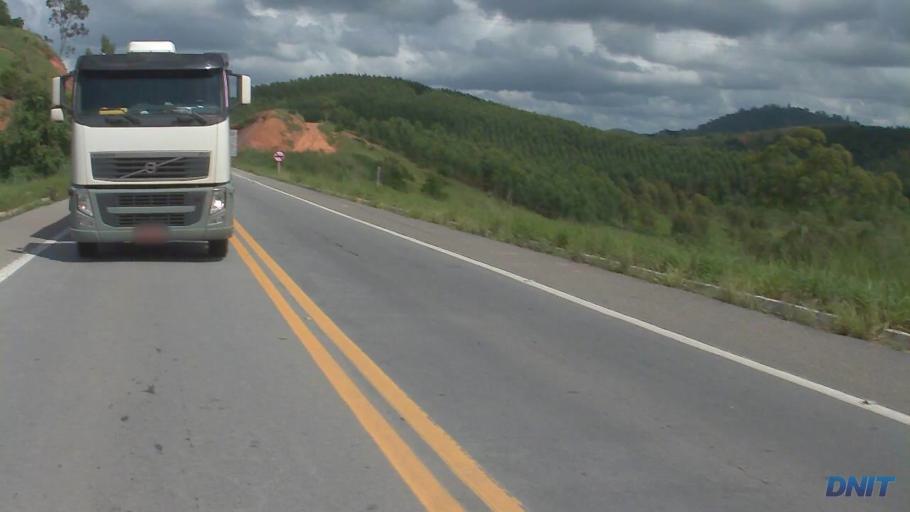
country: BR
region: Minas Gerais
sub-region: Governador Valadares
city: Governador Valadares
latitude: -19.0692
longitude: -42.1744
